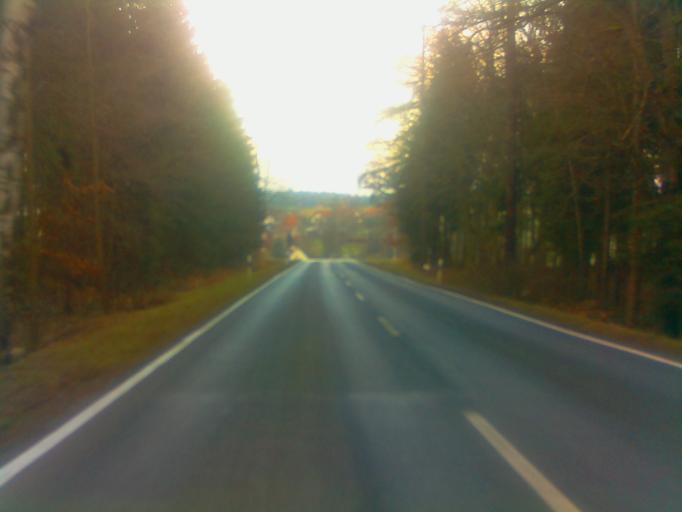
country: DE
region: Thuringia
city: Trockenborn-Wolfersdorf
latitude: 50.7547
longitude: 11.7040
